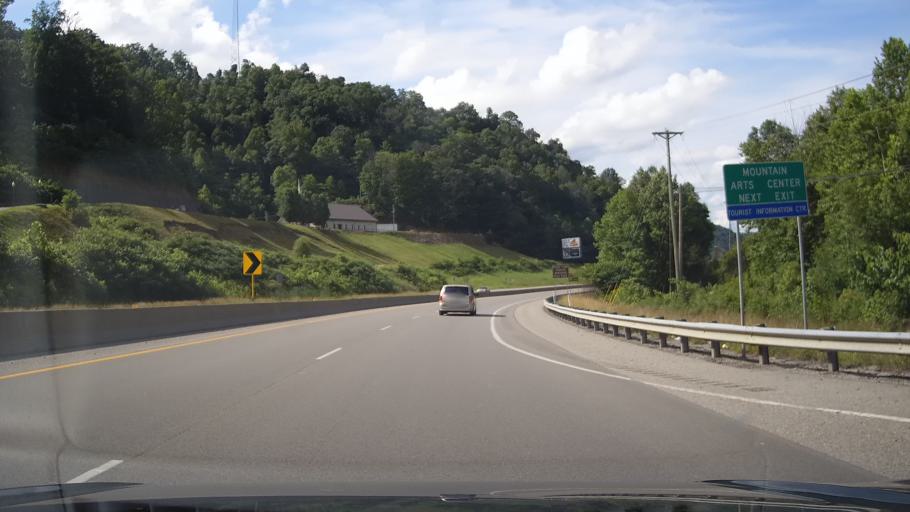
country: US
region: Kentucky
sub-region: Floyd County
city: Prestonsburg
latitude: 37.6511
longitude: -82.7853
